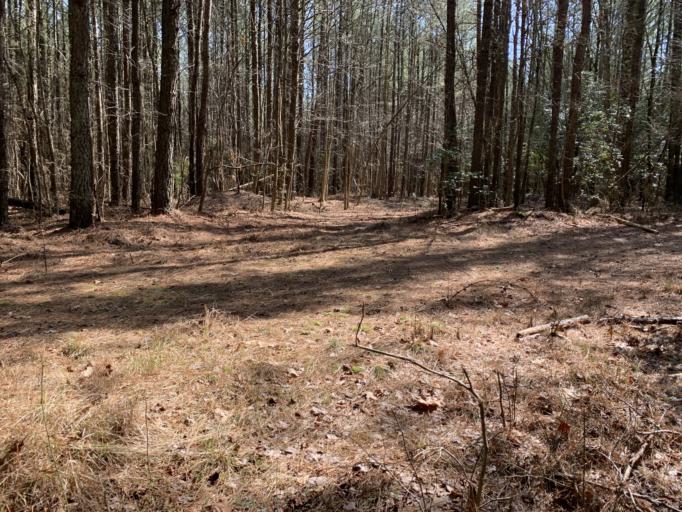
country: US
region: Delaware
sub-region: Sussex County
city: Georgetown
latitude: 38.6785
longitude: -75.4741
